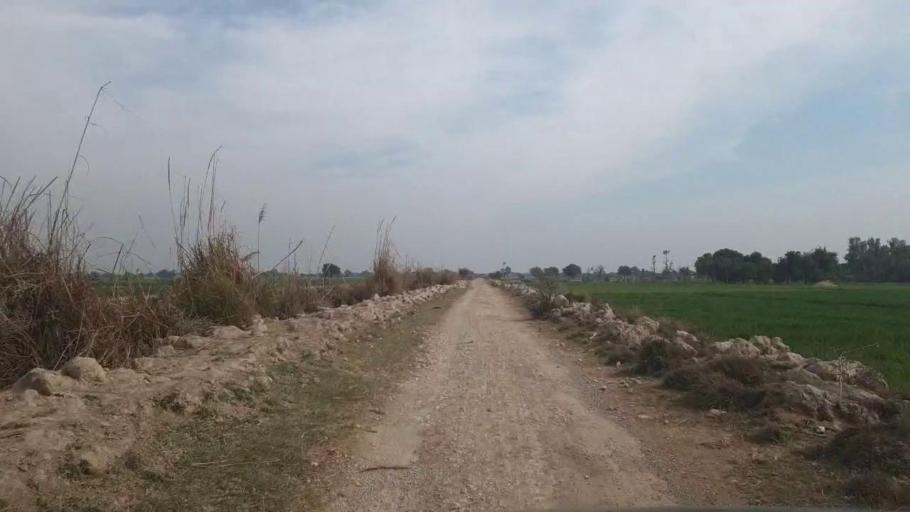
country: PK
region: Sindh
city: Nawabshah
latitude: 26.0754
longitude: 68.4553
